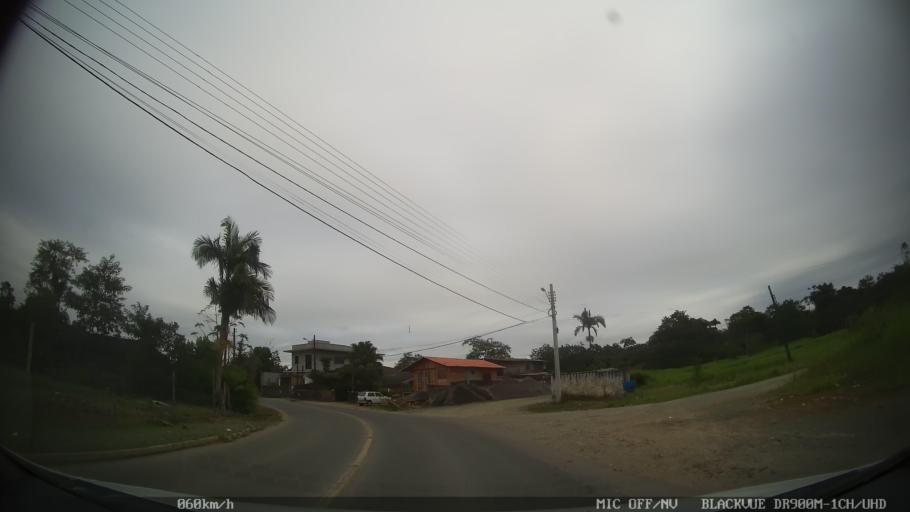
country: BR
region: Santa Catarina
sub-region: Joinville
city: Joinville
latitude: -26.3358
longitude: -48.9099
